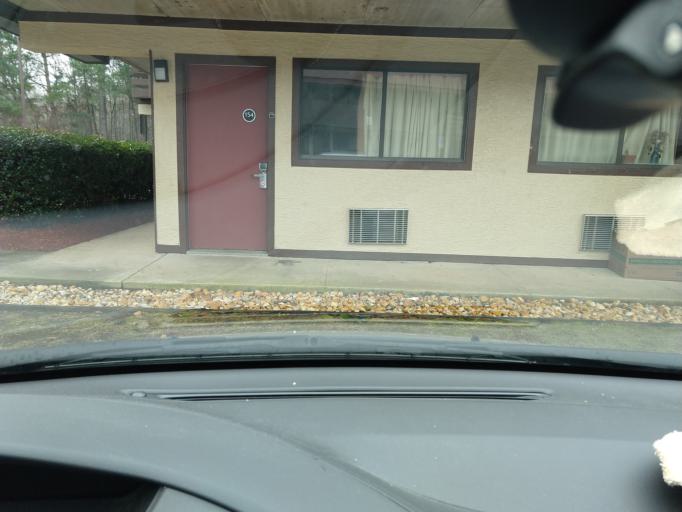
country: US
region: South Carolina
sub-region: Greenville County
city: Mauldin
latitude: 34.8136
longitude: -82.3330
